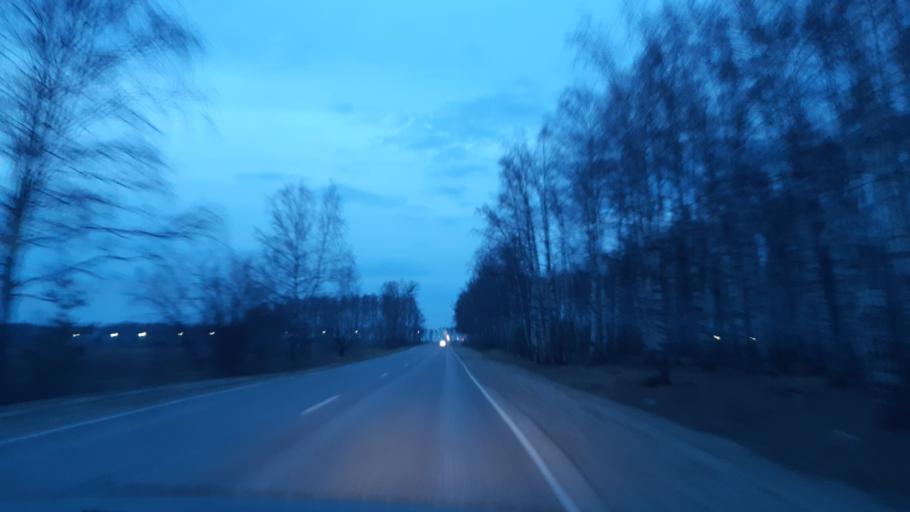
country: RU
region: Vladimir
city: Luknovo
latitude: 56.2318
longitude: 42.0345
